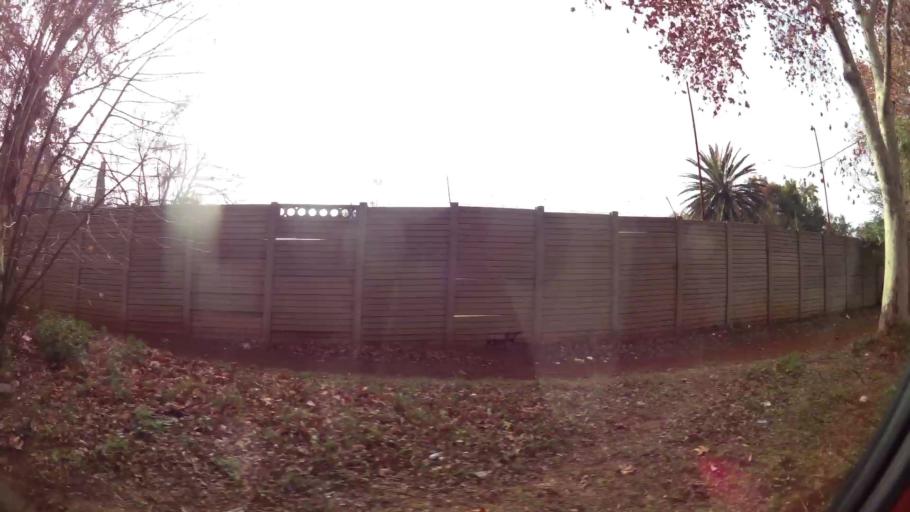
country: ZA
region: Gauteng
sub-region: Sedibeng District Municipality
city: Vanderbijlpark
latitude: -26.7014
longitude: 27.8160
